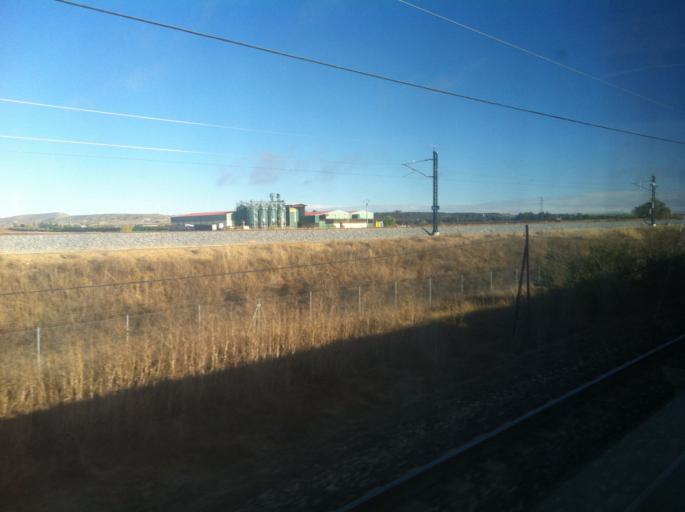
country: ES
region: Castille and Leon
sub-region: Provincia de Palencia
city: Villodrigo
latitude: 42.1527
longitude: -4.0965
